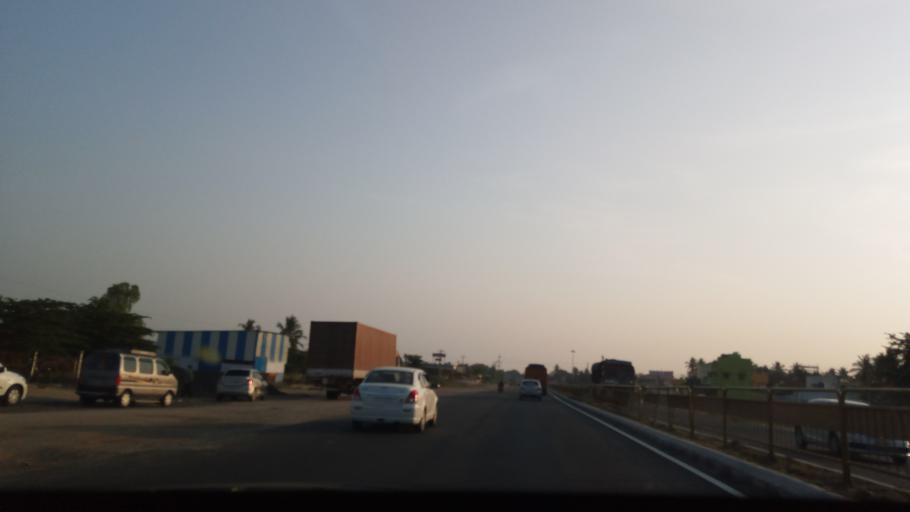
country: IN
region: Tamil Nadu
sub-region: Salem
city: Omalur
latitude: 11.8468
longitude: 78.0685
